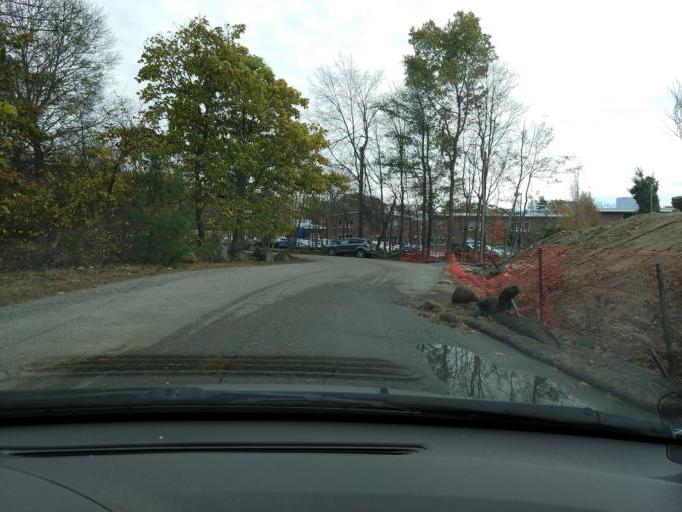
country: US
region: Massachusetts
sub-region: Middlesex County
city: Bedford
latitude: 42.4918
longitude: -71.2872
